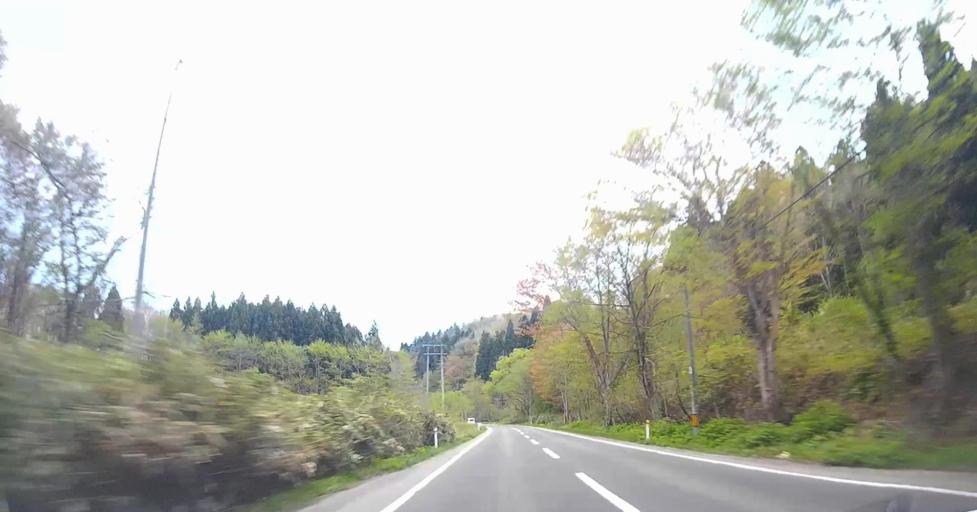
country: JP
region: Aomori
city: Goshogawara
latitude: 41.1267
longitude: 140.5196
